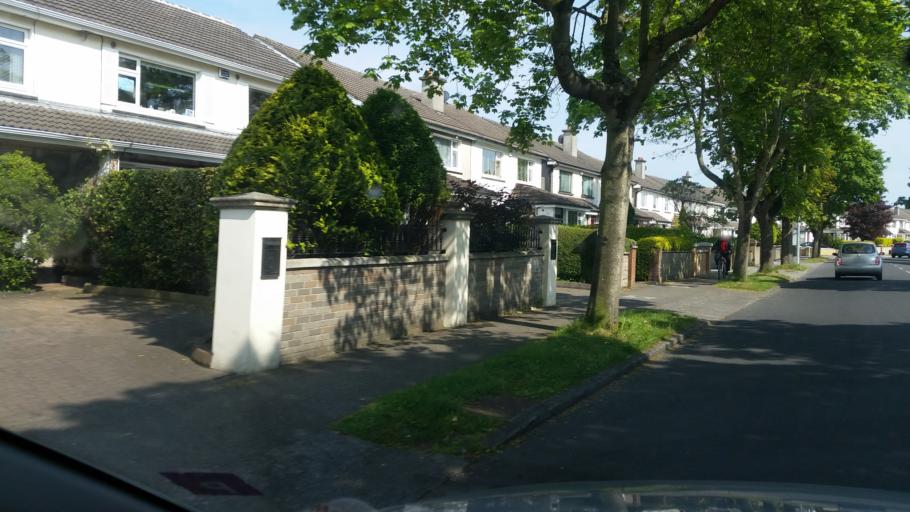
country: IE
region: Leinster
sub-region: Fingal County
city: Blanchardstown
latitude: 53.3853
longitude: -6.3833
